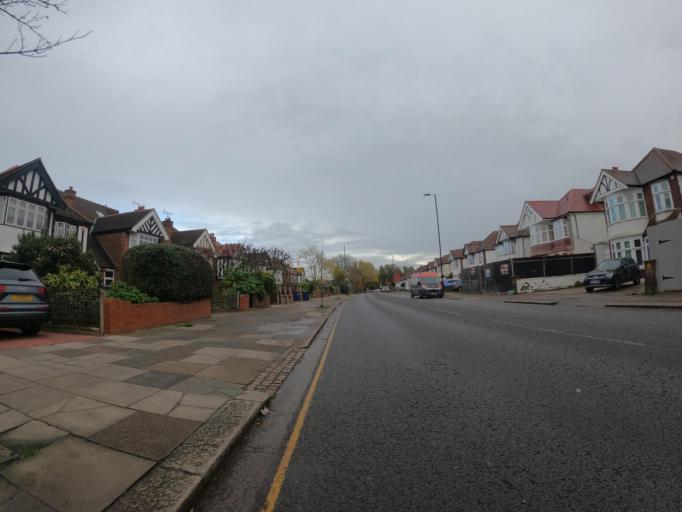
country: GB
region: England
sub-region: Greater London
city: Ealing
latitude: 51.5016
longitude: -0.2916
